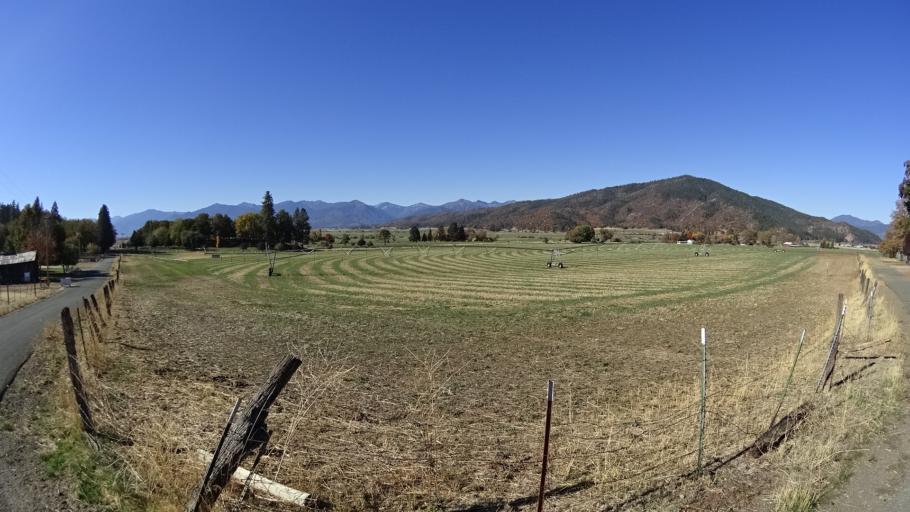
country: US
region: California
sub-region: Siskiyou County
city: Yreka
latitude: 41.5929
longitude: -122.8328
